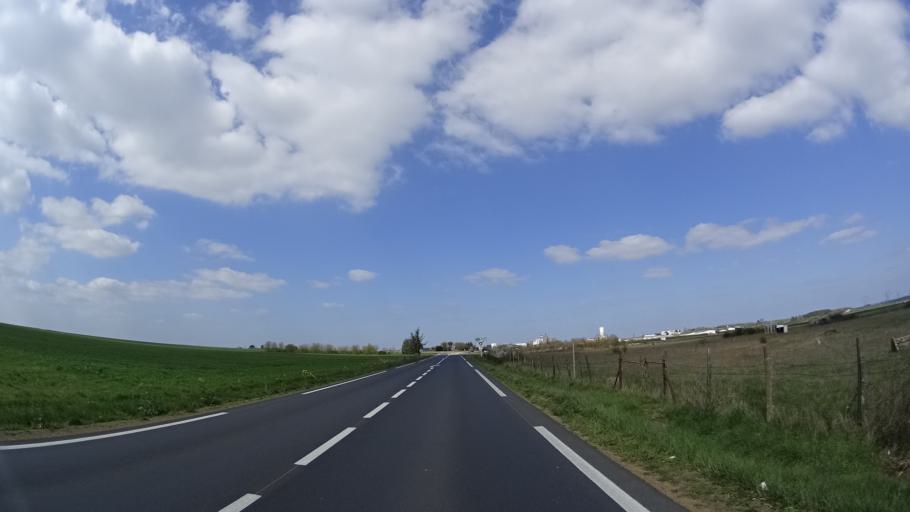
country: FR
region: Pays de la Loire
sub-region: Departement de Maine-et-Loire
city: Montreuil-Bellay
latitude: 47.1164
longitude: -0.1279
